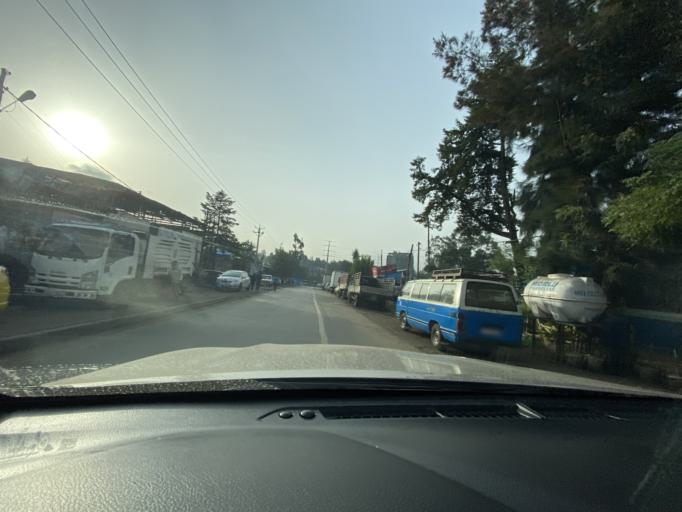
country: ET
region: Adis Abeba
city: Addis Ababa
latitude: 9.0195
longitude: 38.7251
